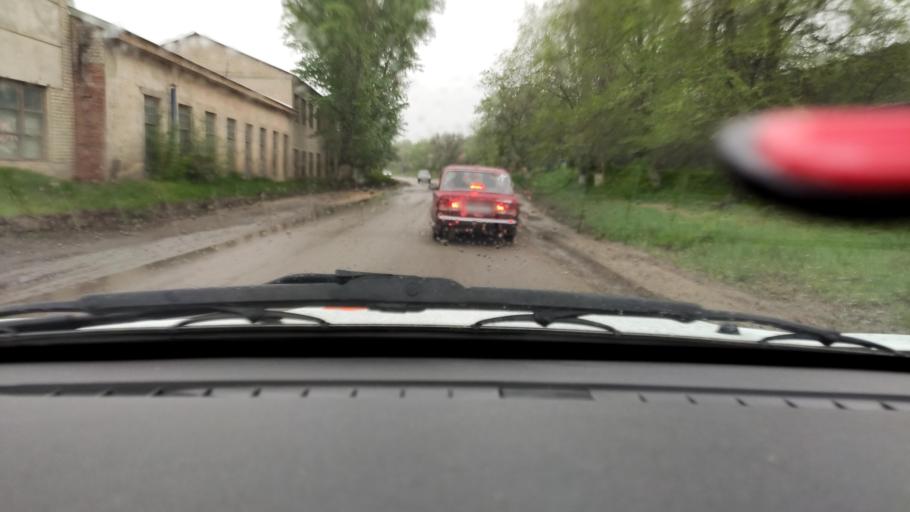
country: RU
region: Voronezj
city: Strelitsa
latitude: 51.6151
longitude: 38.9034
